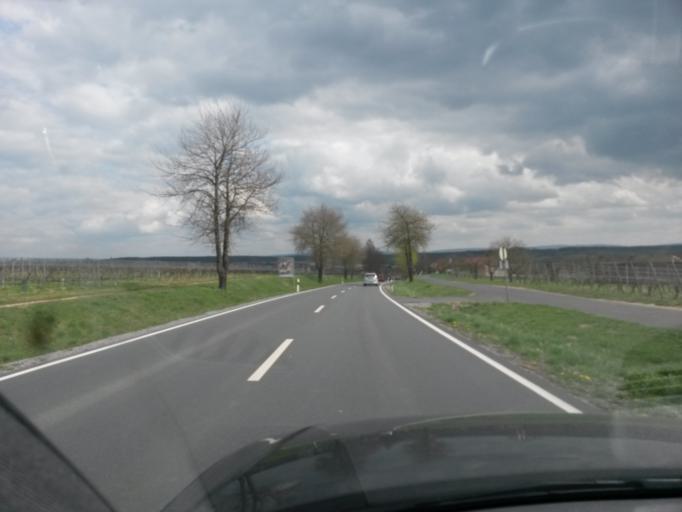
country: DE
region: Bavaria
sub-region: Regierungsbezirk Unterfranken
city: Volkach
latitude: 49.8647
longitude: 10.2073
